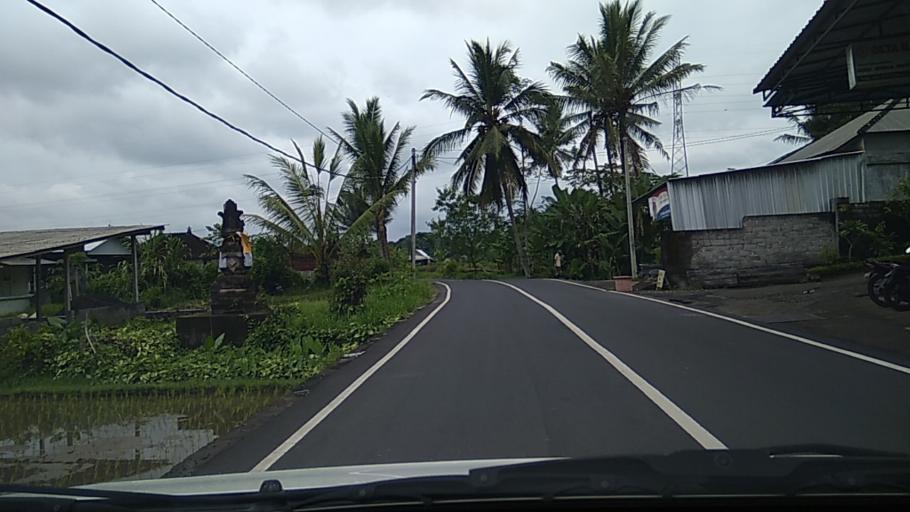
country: ID
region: Bali
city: Brahmana
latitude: -8.4731
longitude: 115.1979
